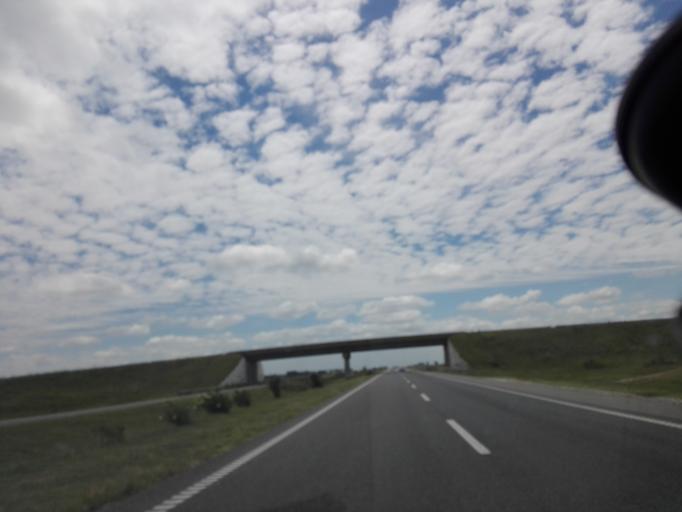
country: AR
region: Cordoba
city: Oliva
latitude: -31.9903
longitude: -63.5628
